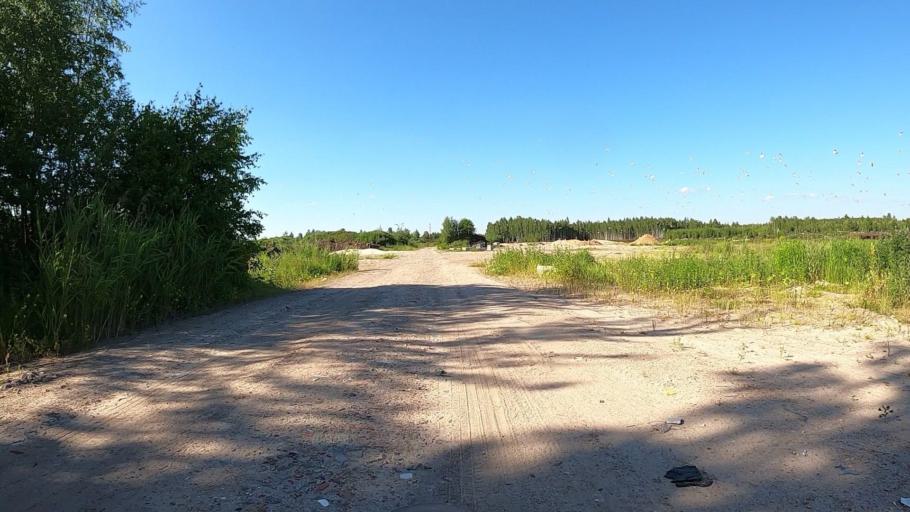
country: LV
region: Stopini
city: Ulbroka
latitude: 56.8825
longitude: 24.2785
